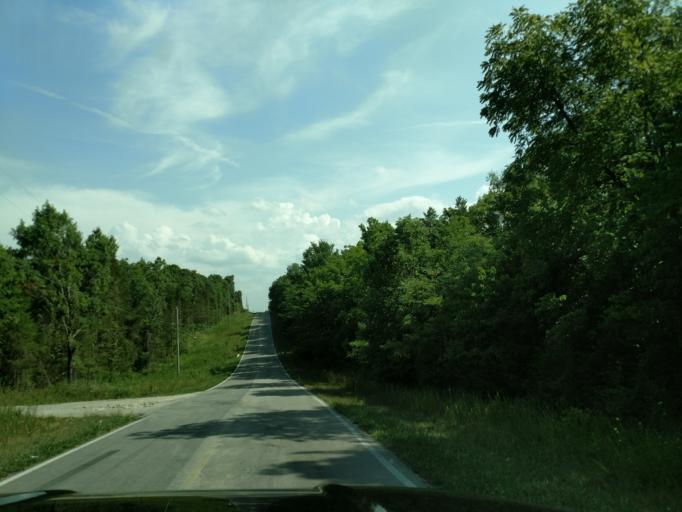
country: US
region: Missouri
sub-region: Barry County
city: Shell Knob
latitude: 36.6065
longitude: -93.5812
